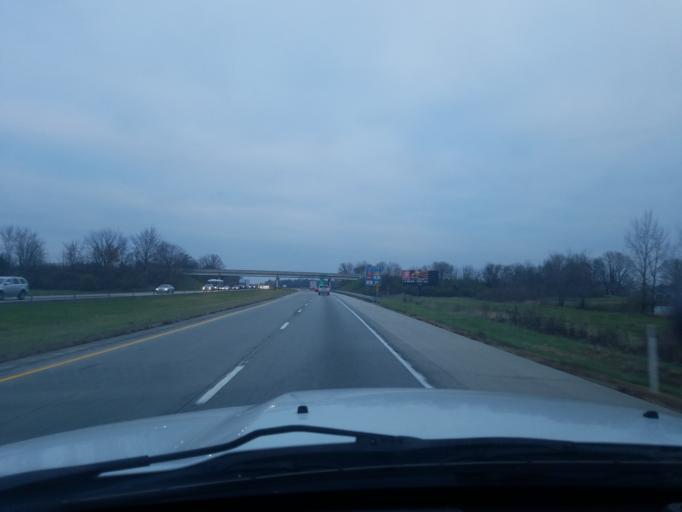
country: US
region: Indiana
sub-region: Madison County
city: Chesterfield
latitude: 40.0902
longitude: -85.5718
